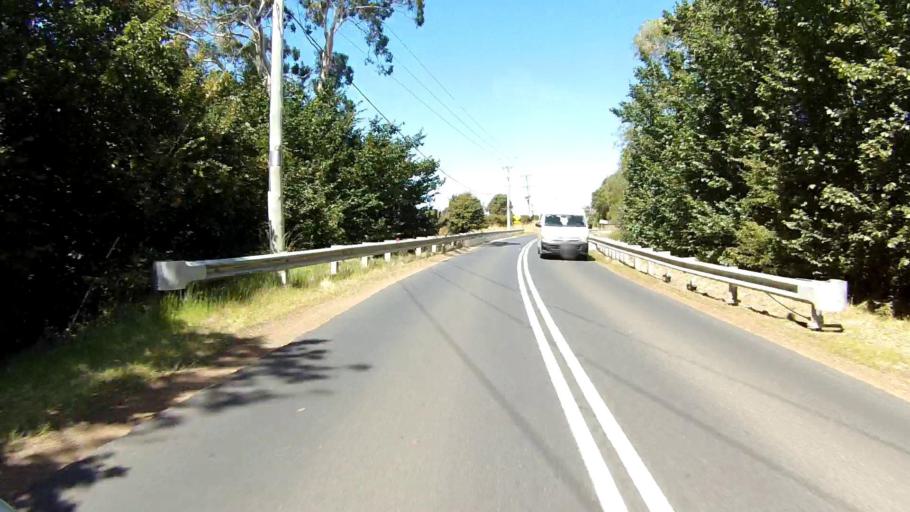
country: AU
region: Tasmania
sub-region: Break O'Day
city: St Helens
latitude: -42.1156
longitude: 148.0606
